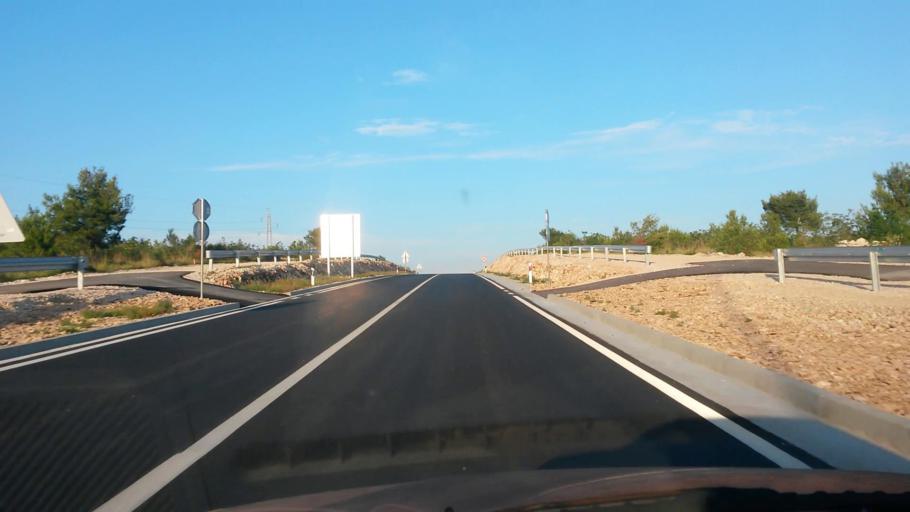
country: HR
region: Sibensko-Kniniska
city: Vodice
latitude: 43.7752
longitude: 15.7753
